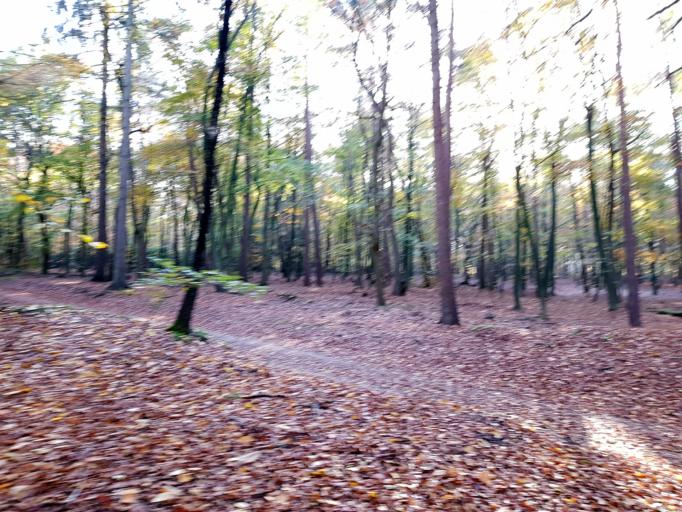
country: NL
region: Gelderland
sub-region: Gemeente Groesbeek
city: Groesbeek
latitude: 51.7760
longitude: 5.9229
